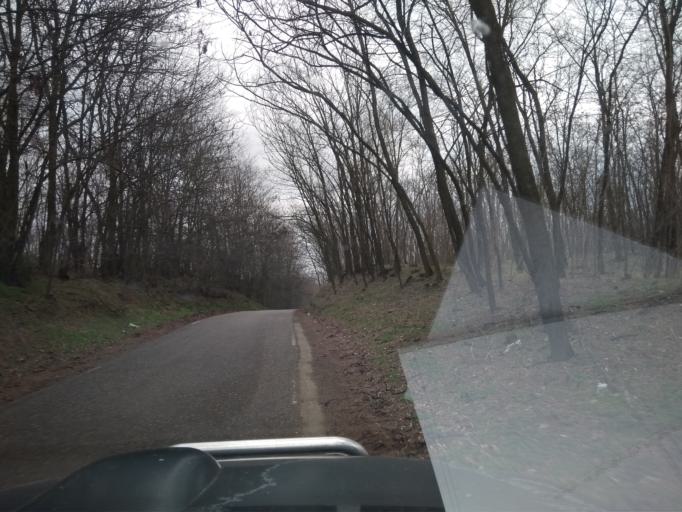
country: HU
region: Szabolcs-Szatmar-Bereg
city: Nyirpazony
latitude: 48.0248
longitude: 21.7973
